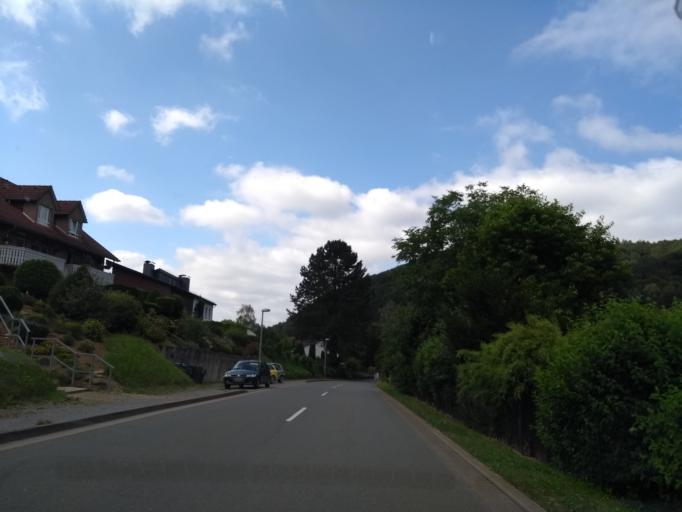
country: DE
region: North Rhine-Westphalia
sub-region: Regierungsbezirk Detmold
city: Lugde
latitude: 51.9553
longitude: 9.2631
